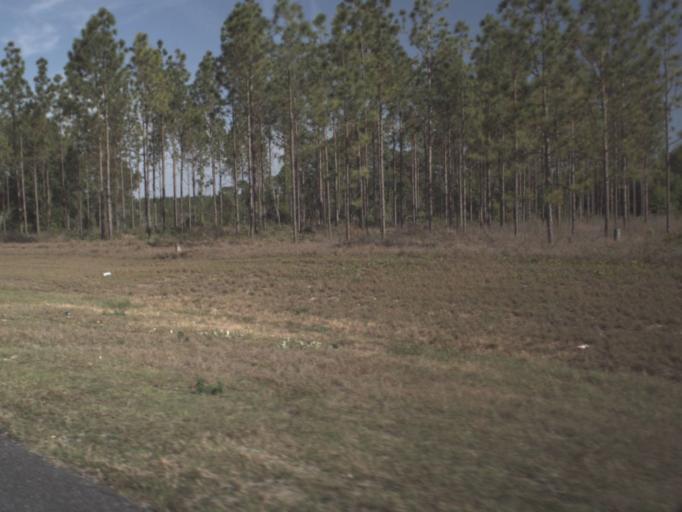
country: US
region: Florida
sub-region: Lake County
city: Mascotte
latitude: 28.6526
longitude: -81.8387
